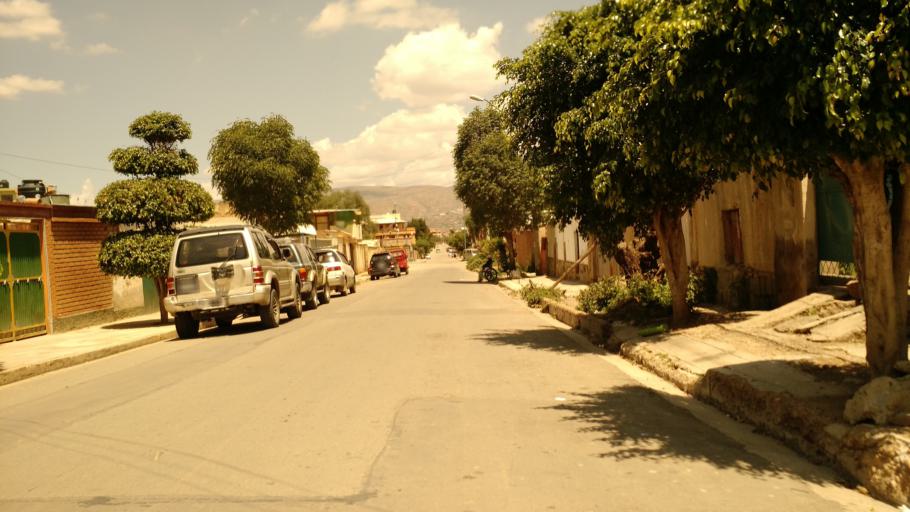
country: BO
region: Cochabamba
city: Cochabamba
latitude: -17.4297
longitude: -66.1539
